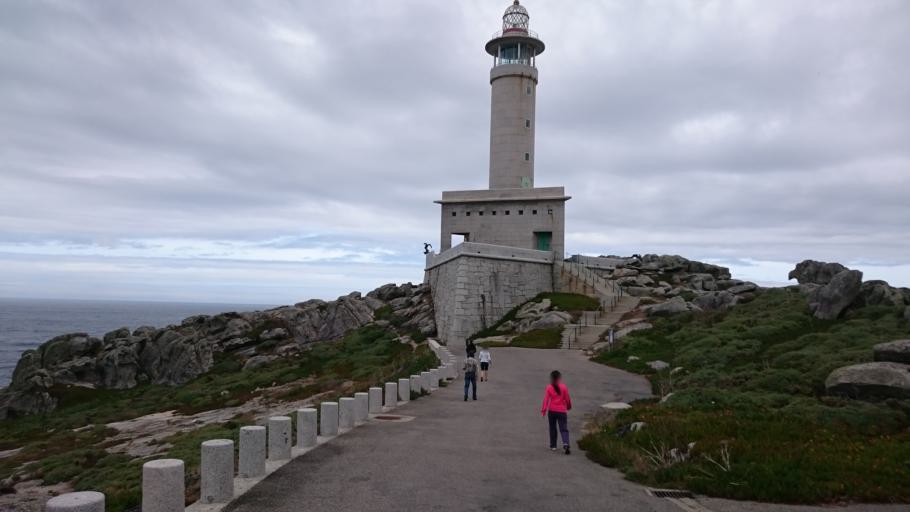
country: ES
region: Galicia
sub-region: Provincia da Coruna
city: Malpica
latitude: 43.3199
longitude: -8.9095
